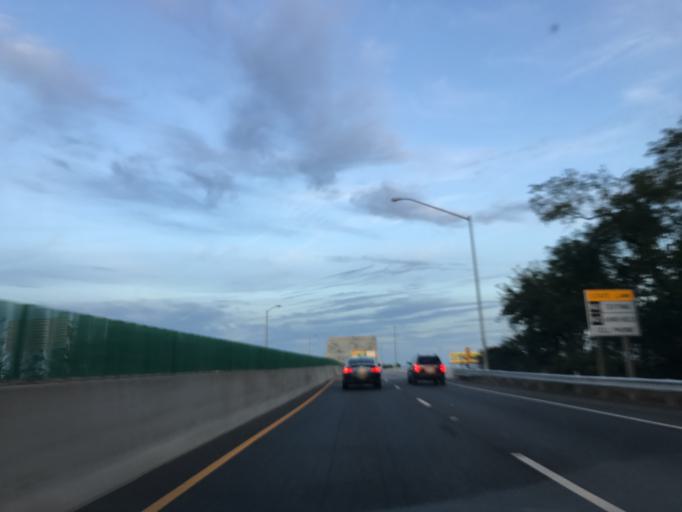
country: US
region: Maryland
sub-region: Anne Arundel County
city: Brooklyn Park
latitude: 39.2411
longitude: -76.6008
